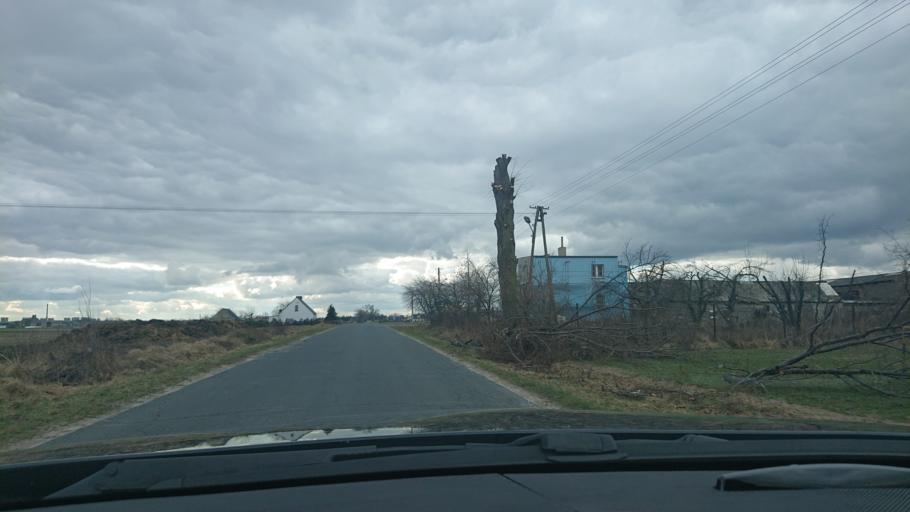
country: PL
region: Greater Poland Voivodeship
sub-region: Powiat gnieznienski
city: Gniezno
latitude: 52.5831
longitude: 17.6481
